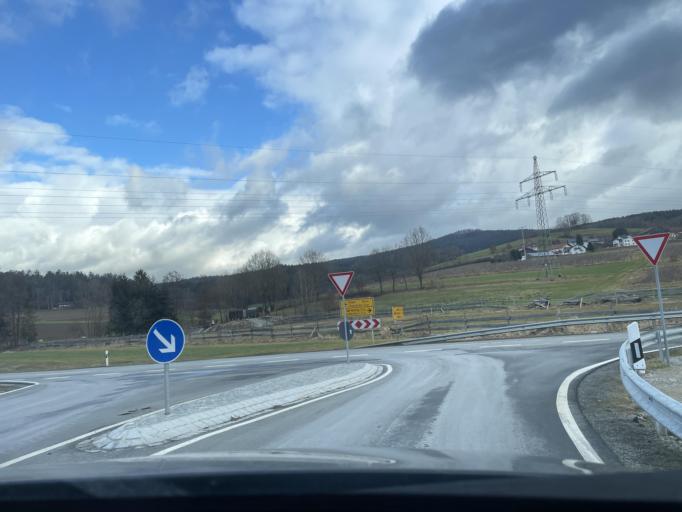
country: DE
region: Bavaria
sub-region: Upper Palatinate
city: Runding
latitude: 49.2001
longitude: 12.7810
